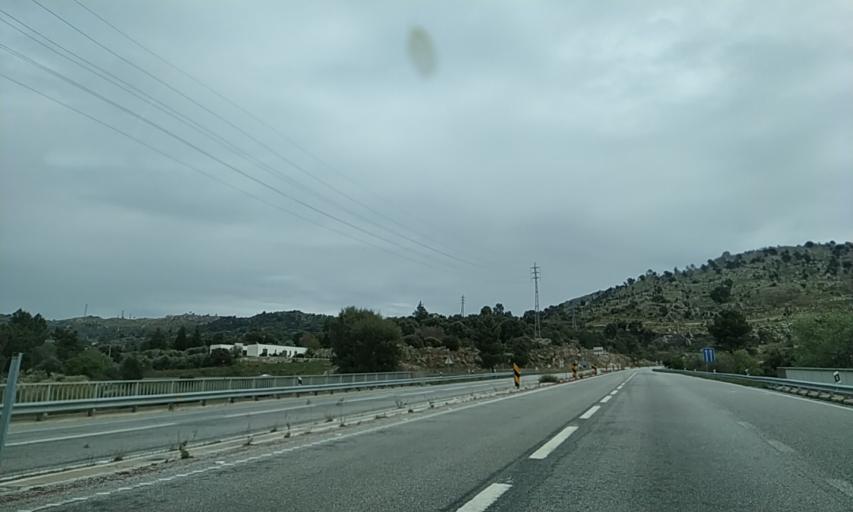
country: PT
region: Guarda
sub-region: Guarda
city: Guarda
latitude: 40.6187
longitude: -7.2859
